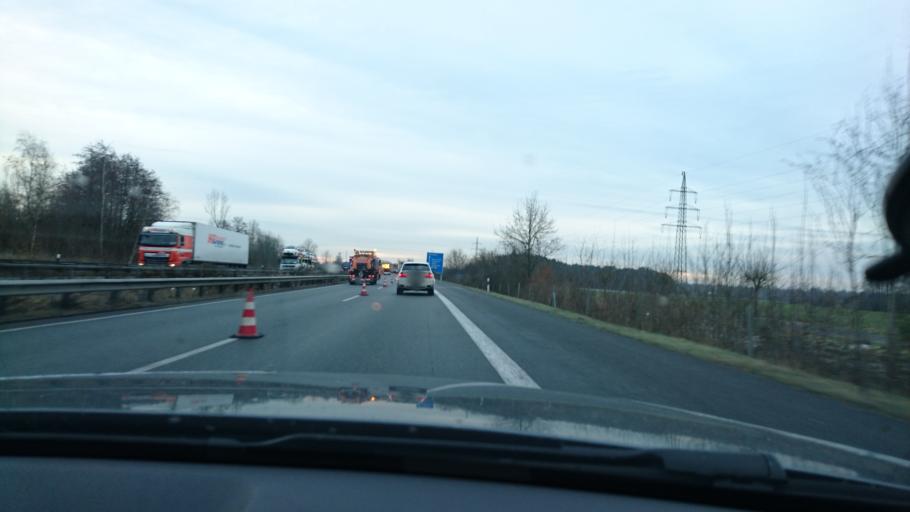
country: DE
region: North Rhine-Westphalia
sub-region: Regierungsbezirk Munster
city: Rheine
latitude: 52.3288
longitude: 7.4195
